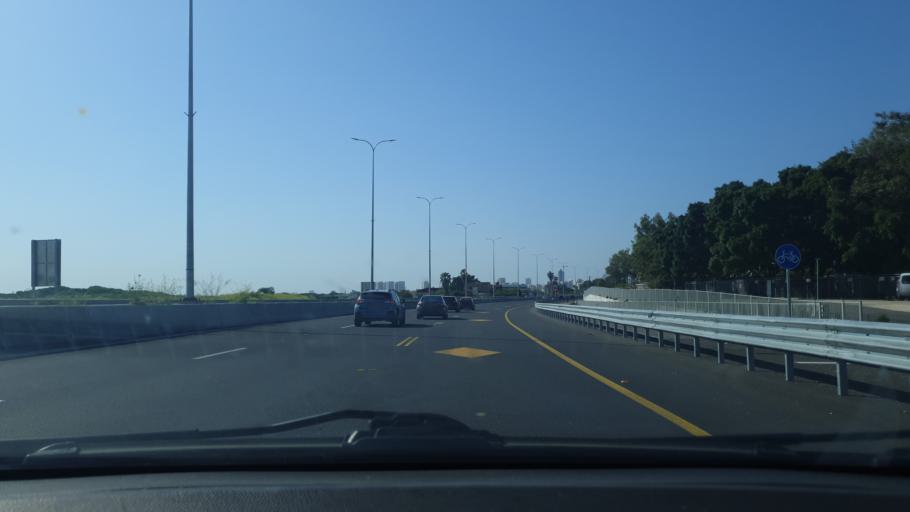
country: IL
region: Tel Aviv
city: Azor
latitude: 32.0387
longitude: 34.8268
